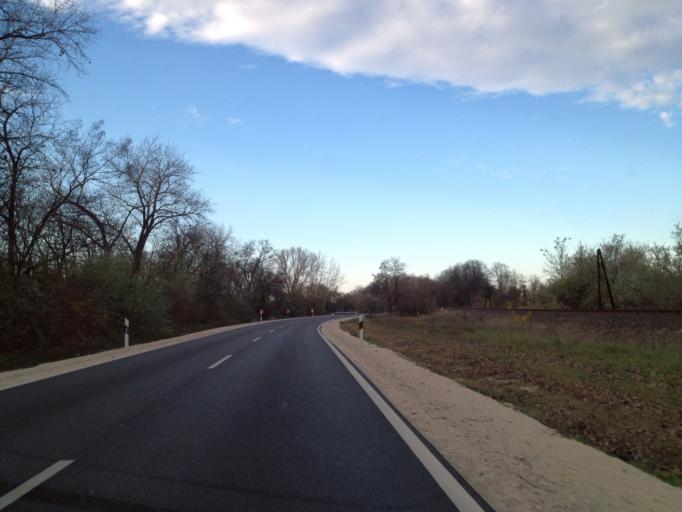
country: HU
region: Gyor-Moson-Sopron
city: Nyul
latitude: 47.6148
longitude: 17.6799
